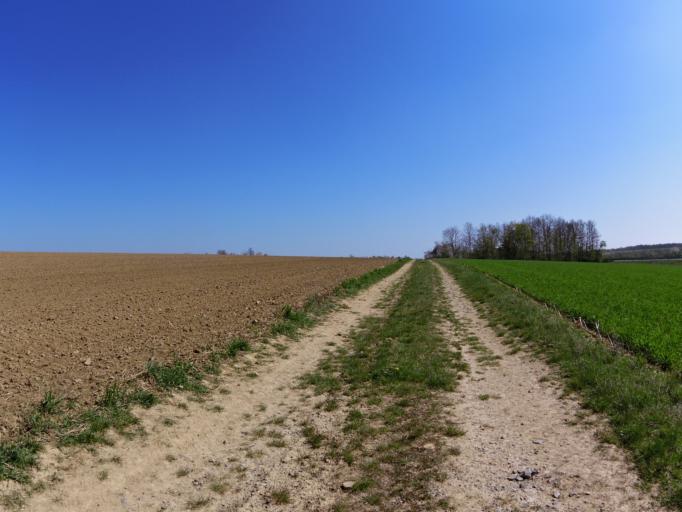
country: DE
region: Bavaria
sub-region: Regierungsbezirk Unterfranken
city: Biebelried
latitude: 49.7780
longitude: 10.0835
